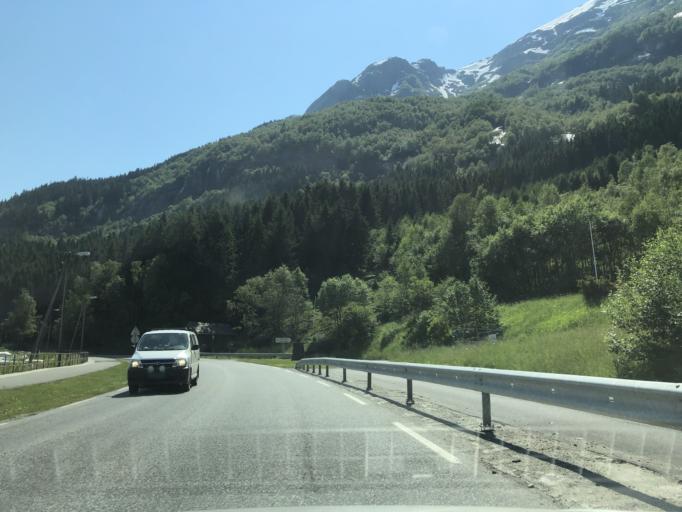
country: NO
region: Hordaland
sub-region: Odda
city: Odda
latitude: 60.0800
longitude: 6.5296
